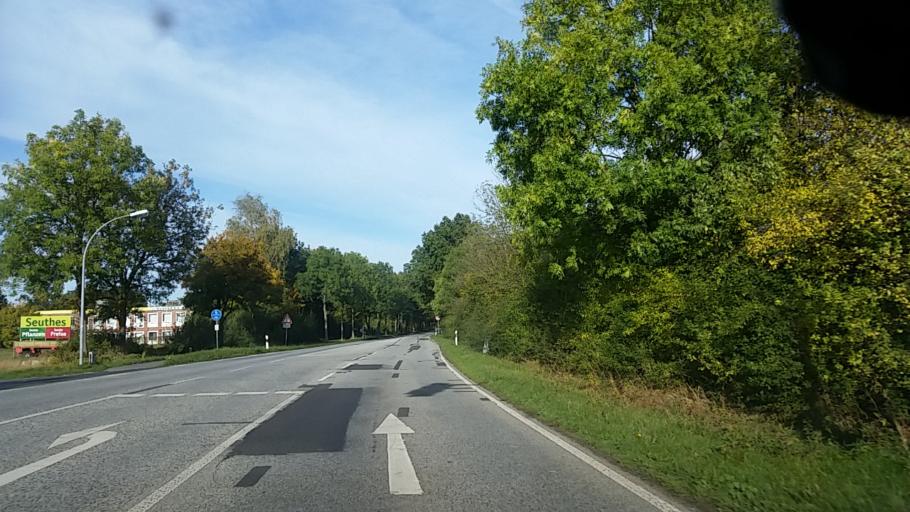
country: DE
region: Schleswig-Holstein
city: Delingsdorf
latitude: 53.6957
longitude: 10.2422
